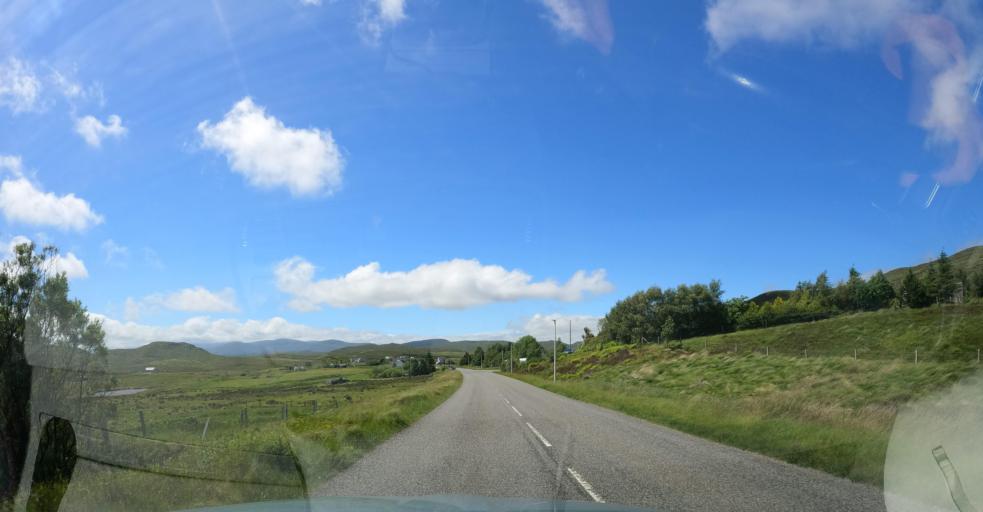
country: GB
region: Scotland
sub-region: Eilean Siar
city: Harris
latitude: 58.0876
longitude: -6.6305
